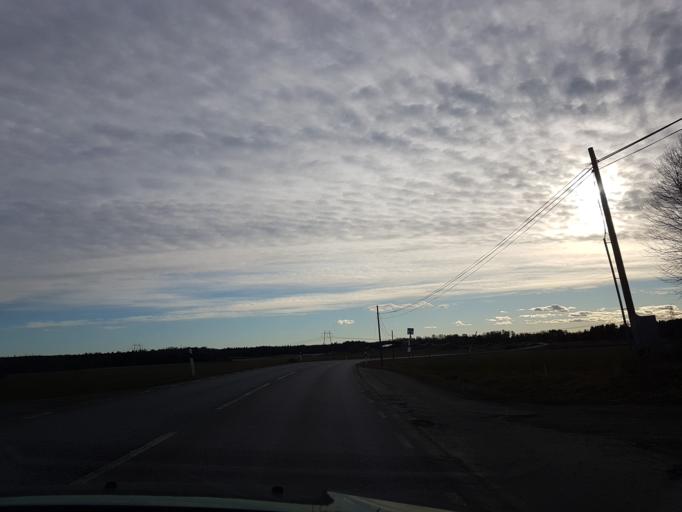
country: SE
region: Stockholm
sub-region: Vallentuna Kommun
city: Vallentuna
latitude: 59.6571
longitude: 18.0426
